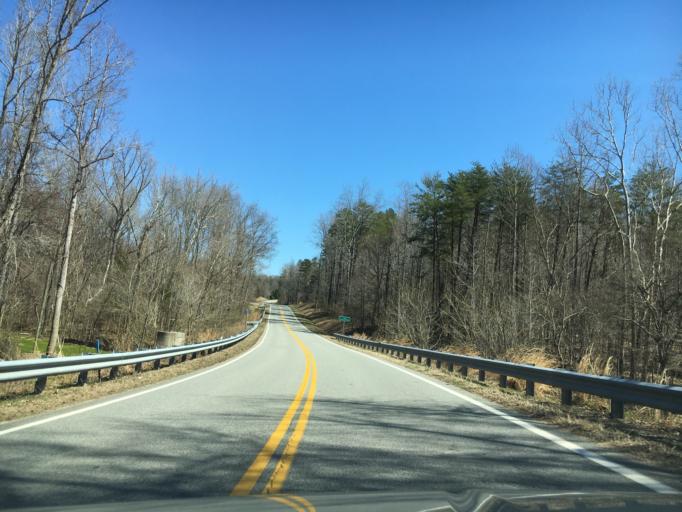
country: US
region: Virginia
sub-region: Halifax County
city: Halifax
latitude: 36.7597
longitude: -78.9070
